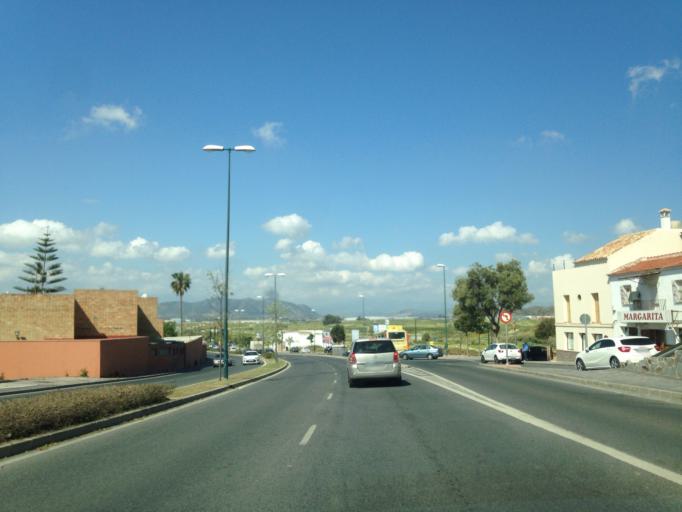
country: ES
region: Andalusia
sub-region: Provincia de Malaga
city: Malaga
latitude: 36.7083
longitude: -4.4882
